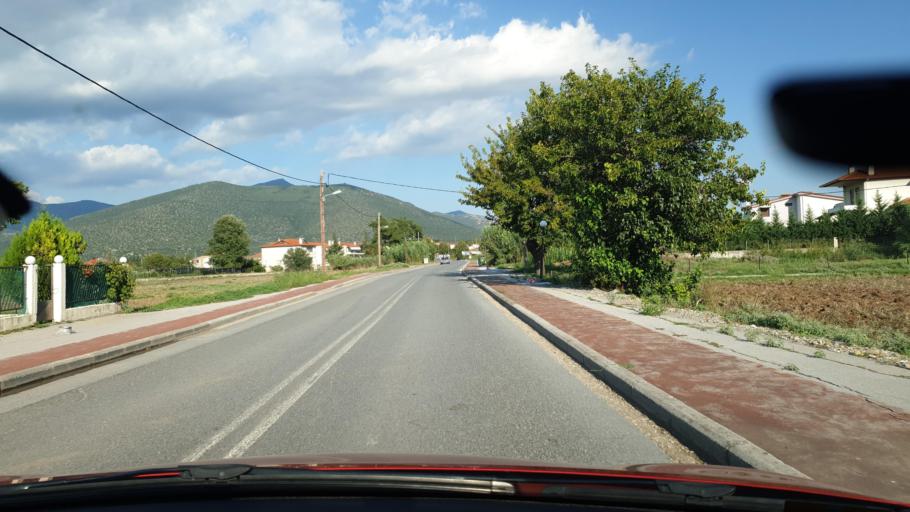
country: GR
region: Central Macedonia
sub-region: Nomos Thessalonikis
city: Vasilika
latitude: 40.4804
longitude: 23.1290
